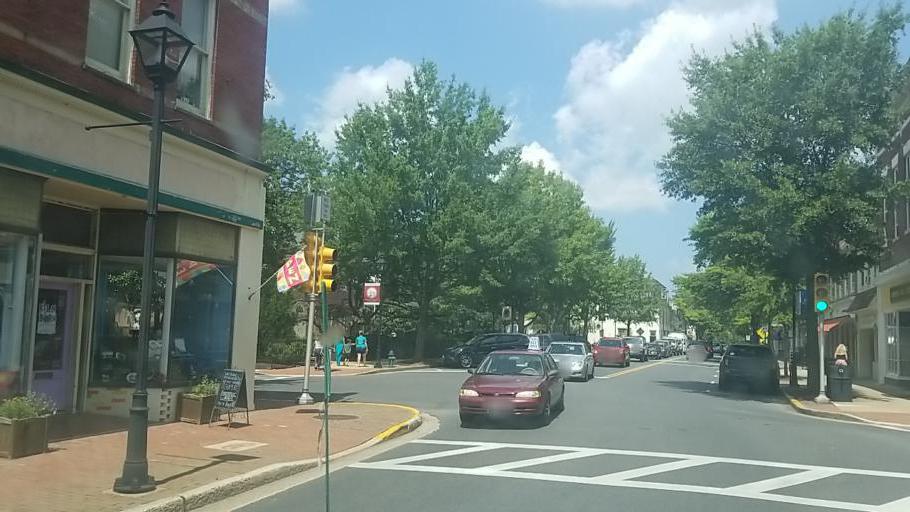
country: US
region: Maryland
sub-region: Talbot County
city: Easton
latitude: 38.7743
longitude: -76.0762
